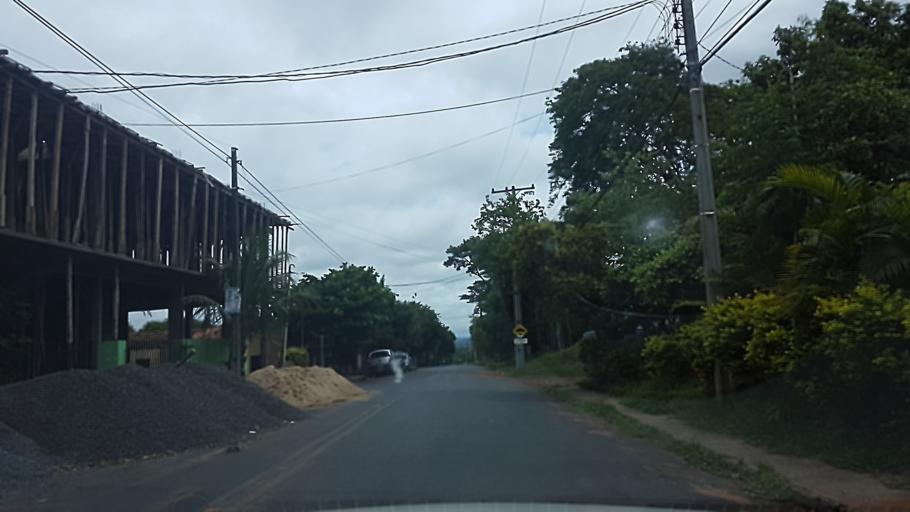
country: PY
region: Central
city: Villa Elisa
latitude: -25.3830
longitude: -57.5855
